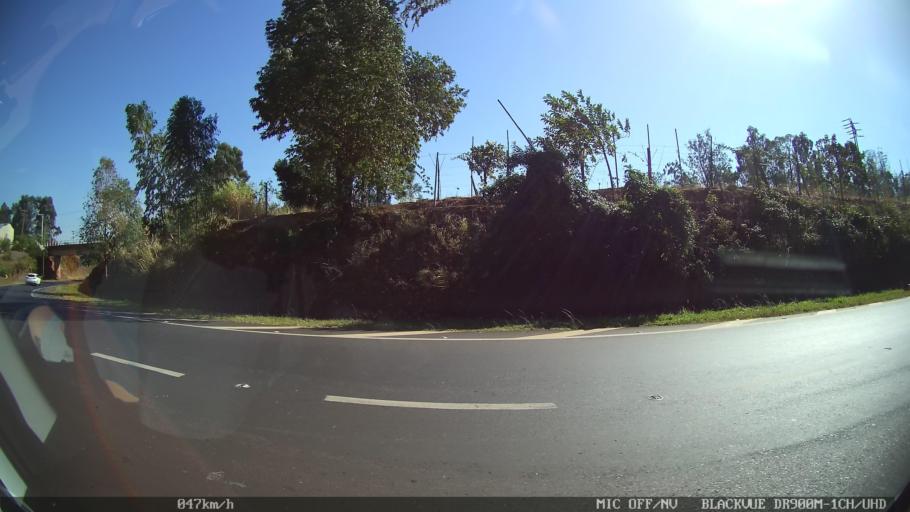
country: BR
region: Sao Paulo
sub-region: Batatais
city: Batatais
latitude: -20.9001
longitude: -47.6069
